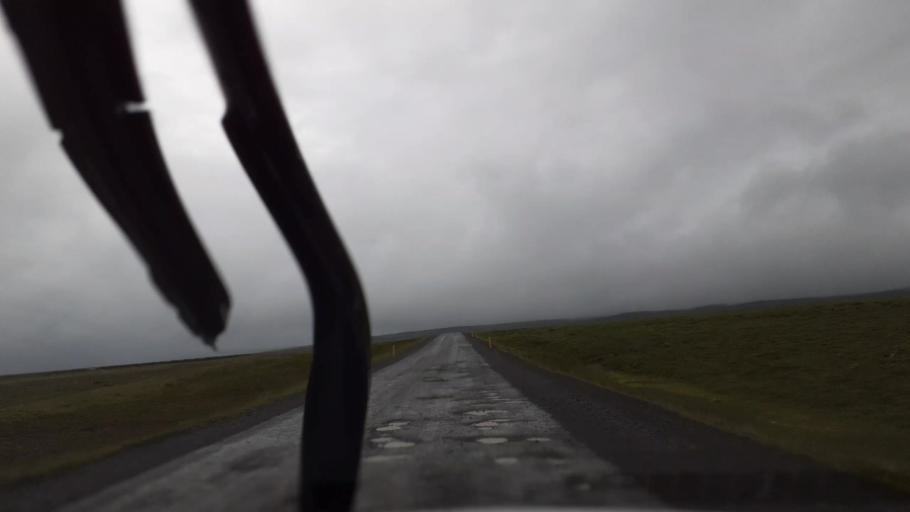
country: IS
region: East
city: Egilsstadir
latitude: 66.0359
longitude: -15.0703
